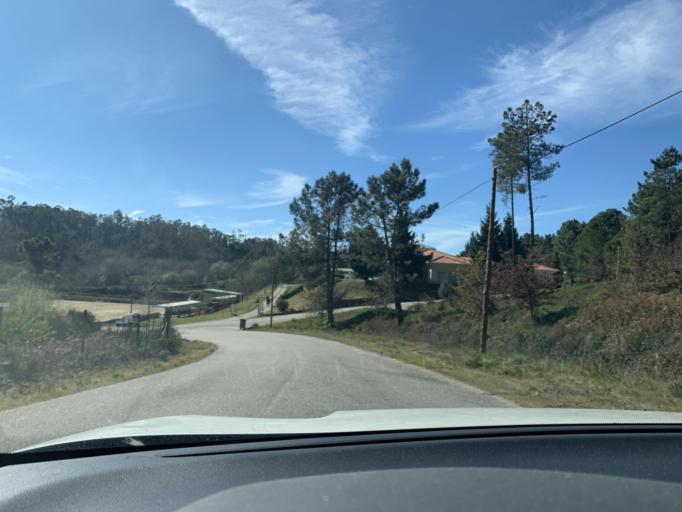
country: PT
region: Viseu
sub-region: Concelho de Tondela
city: Tondela
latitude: 40.6054
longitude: -8.0320
